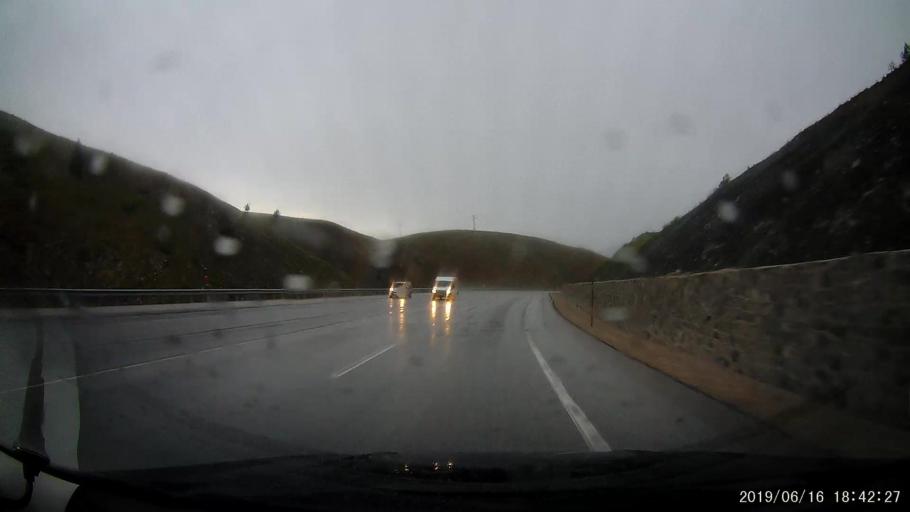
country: TR
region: Erzincan
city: Doganbeyli
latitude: 39.8683
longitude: 39.1091
